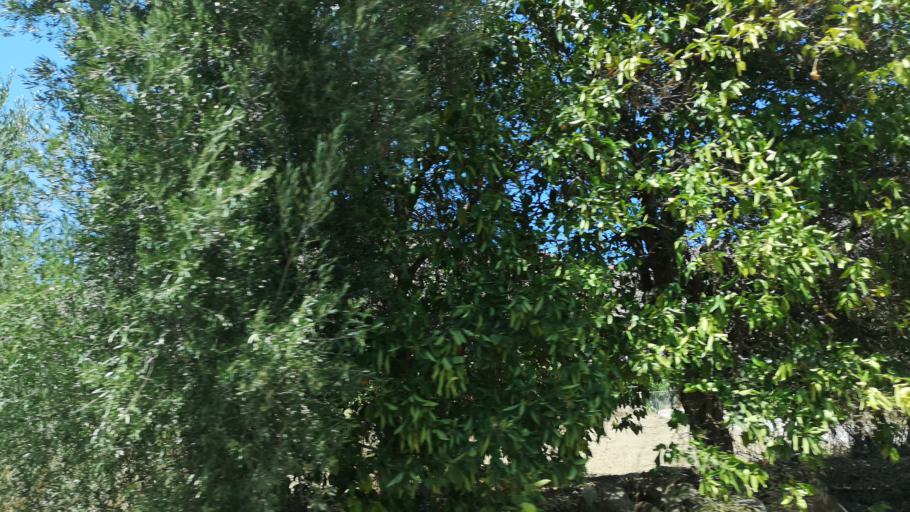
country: GR
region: Crete
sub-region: Nomos Lasithiou
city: Neapoli
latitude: 35.2458
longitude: 25.6349
